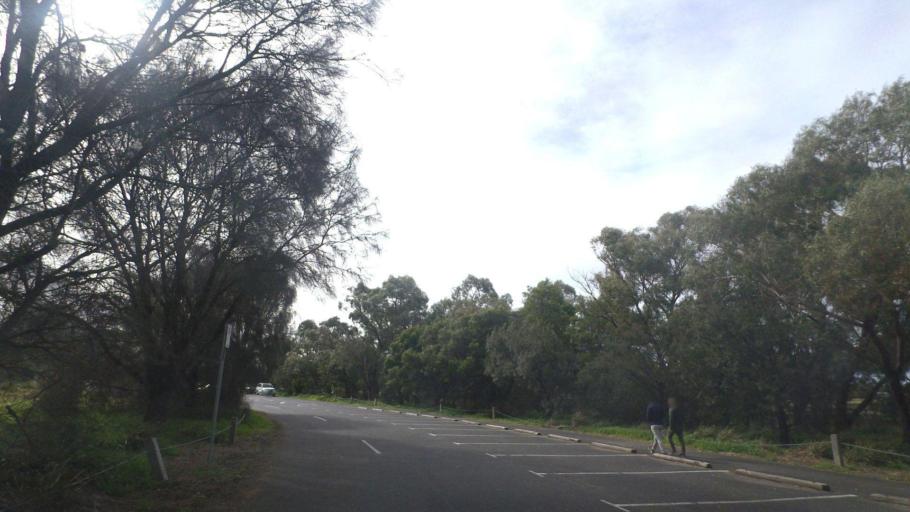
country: AU
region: Victoria
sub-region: Monash
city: Oakleigh South
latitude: -37.9444
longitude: 145.0840
